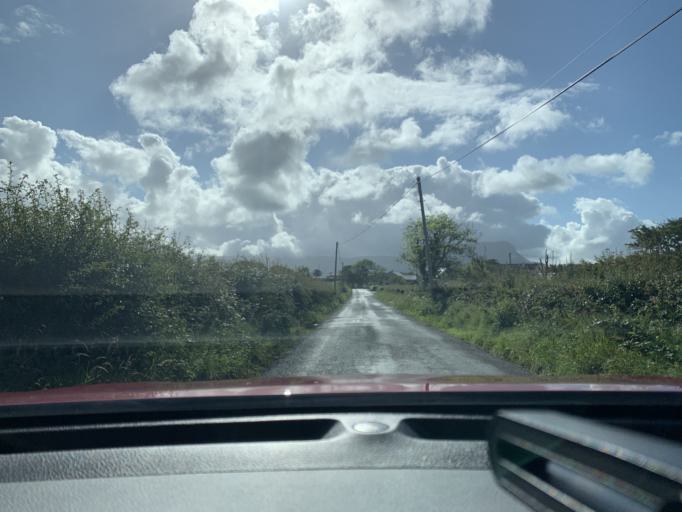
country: IE
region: Connaught
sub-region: Sligo
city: Strandhill
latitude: 54.3919
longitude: -8.5464
